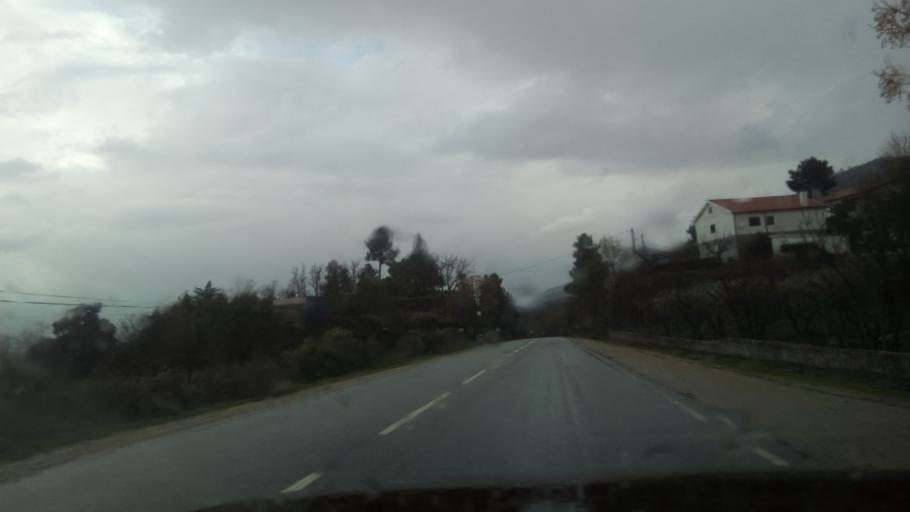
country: PT
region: Guarda
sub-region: Guarda
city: Guarda
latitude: 40.5902
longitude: -7.2900
